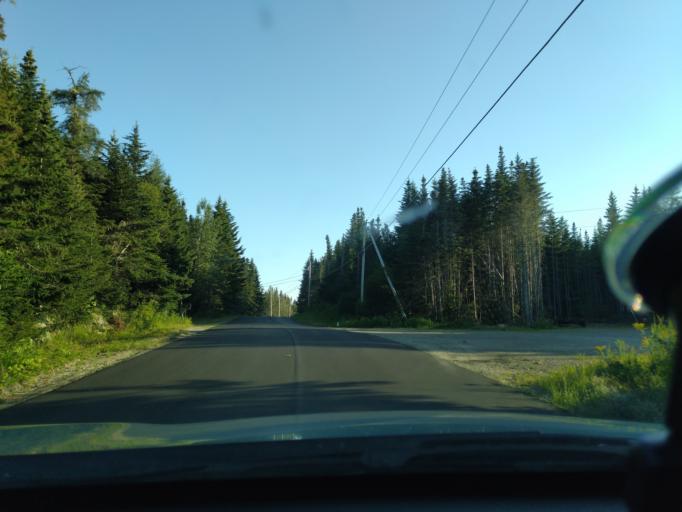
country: US
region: Maine
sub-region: Washington County
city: Machiasport
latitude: 44.6672
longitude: -67.2010
